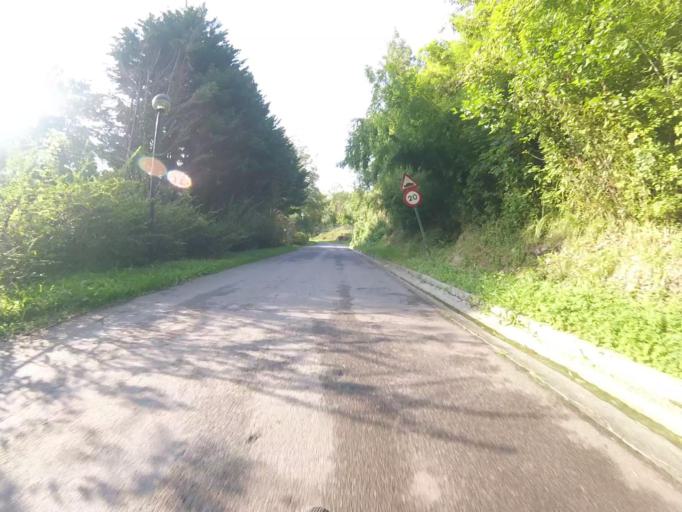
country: ES
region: Basque Country
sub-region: Provincia de Guipuzcoa
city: Irun
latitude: 43.3358
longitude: -1.8321
